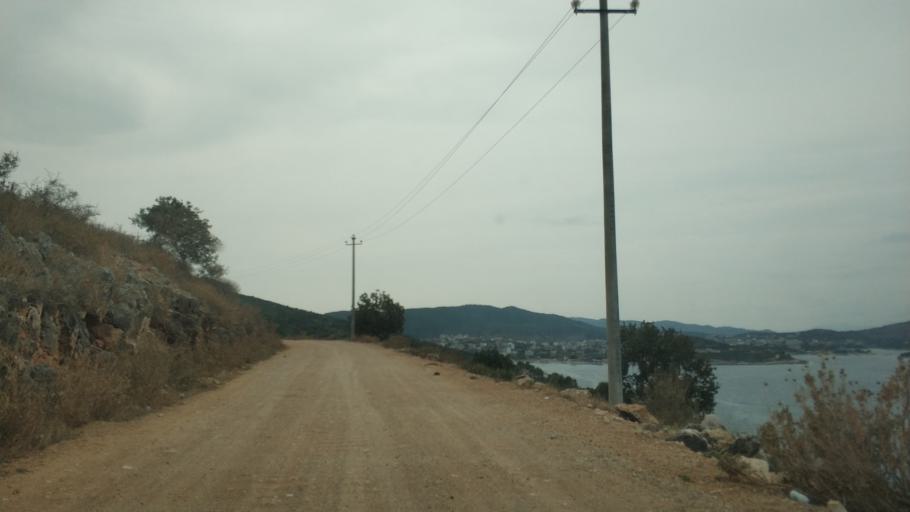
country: AL
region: Vlore
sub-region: Rrethi i Sarandes
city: Xarre
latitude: 39.7926
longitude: 20.0052
